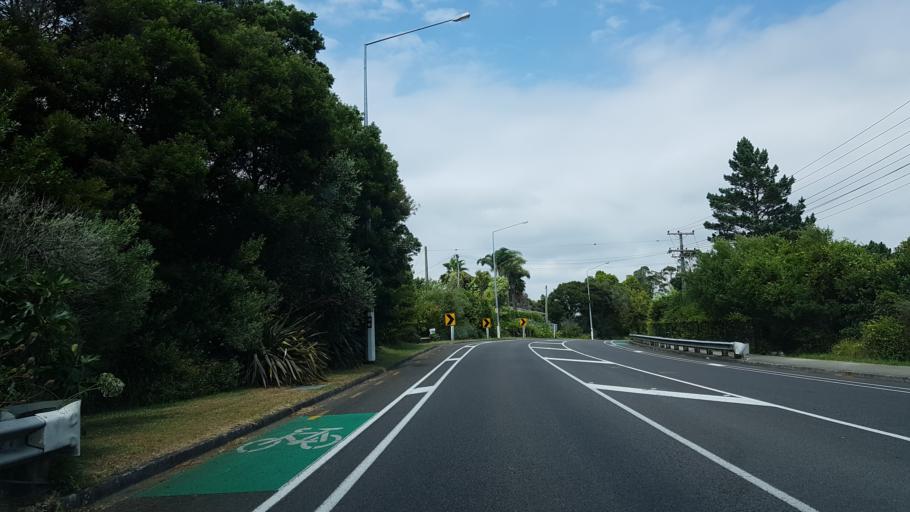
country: NZ
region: Auckland
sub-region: Auckland
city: North Shore
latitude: -36.7795
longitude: 174.6826
